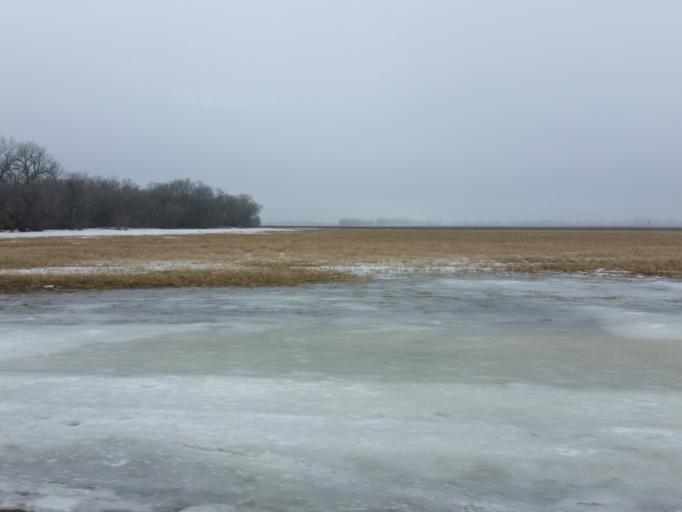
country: US
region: North Dakota
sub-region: Walsh County
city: Grafton
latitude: 48.6248
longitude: -97.4490
